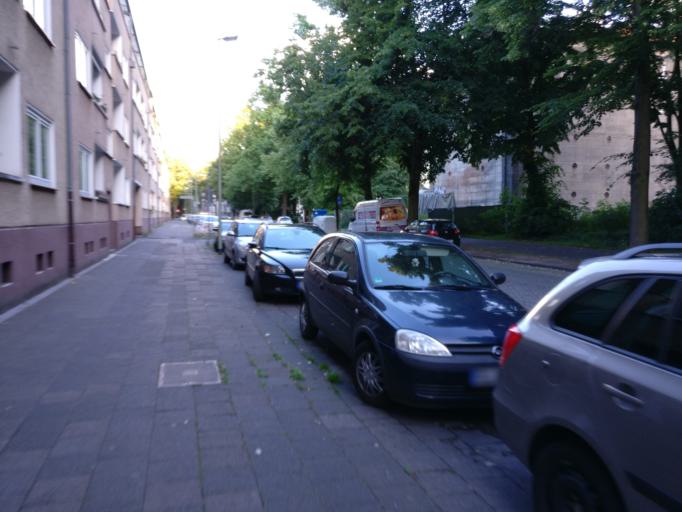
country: DE
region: North Rhine-Westphalia
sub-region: Regierungsbezirk Dusseldorf
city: Duisburg
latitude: 51.4232
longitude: 6.7903
